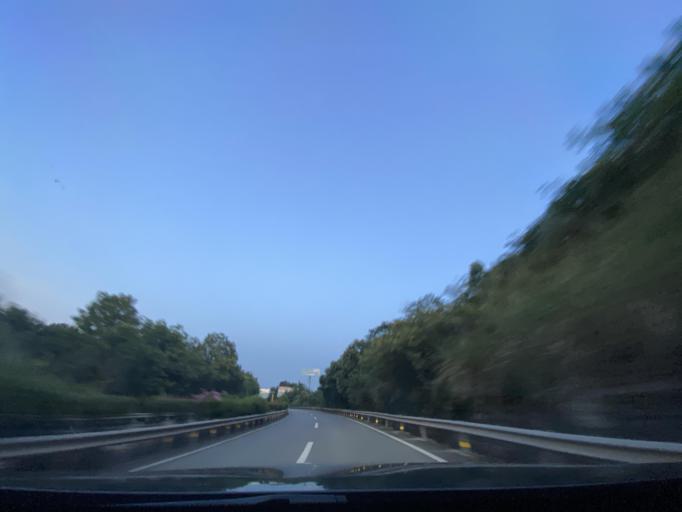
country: CN
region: Sichuan
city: Longquan
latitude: 30.4882
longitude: 104.3926
